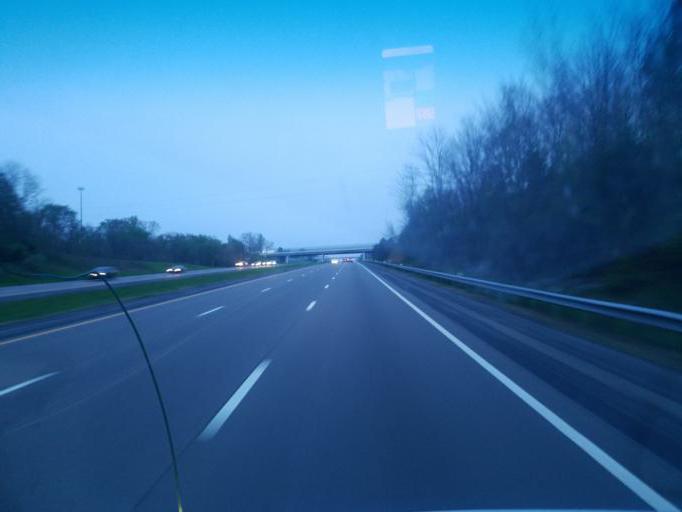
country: US
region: Ohio
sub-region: Medina County
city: Medina
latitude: 41.0976
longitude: -81.8241
